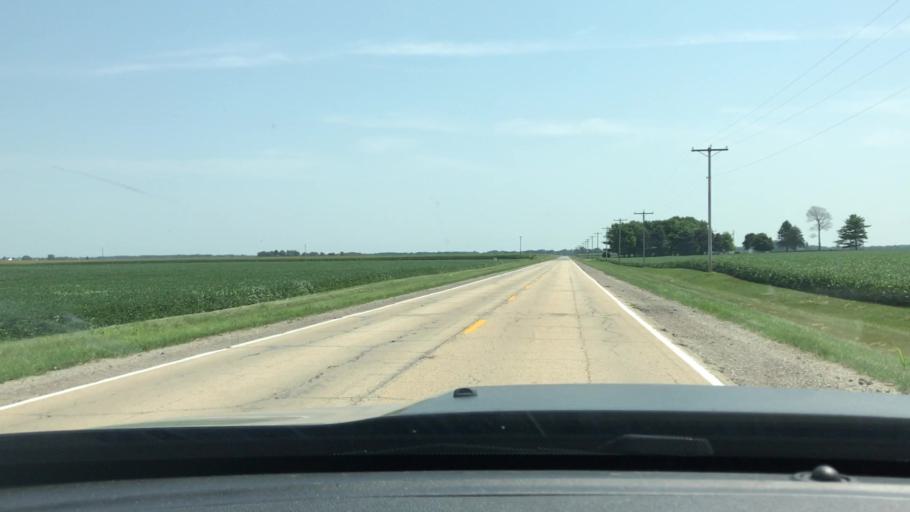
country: US
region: Illinois
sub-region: LaSalle County
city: Sheridan
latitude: 41.4853
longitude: -88.8053
